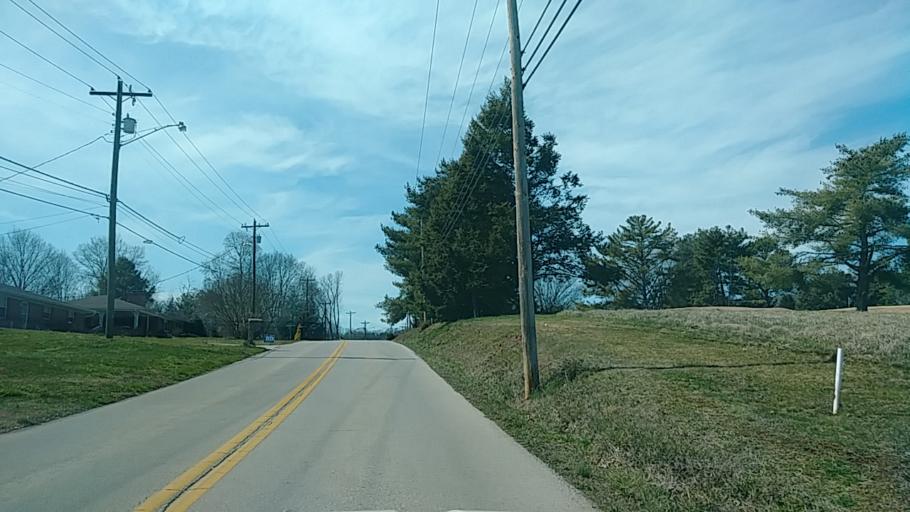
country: US
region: Tennessee
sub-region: Hamblen County
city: Morristown
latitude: 36.2123
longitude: -83.3284
